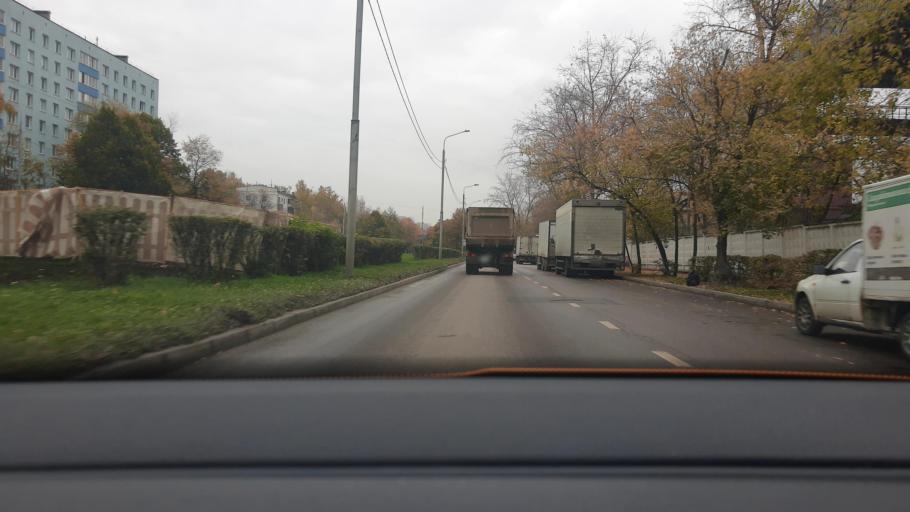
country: RU
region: Moscow
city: Metrogorodok
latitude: 55.8190
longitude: 37.7574
